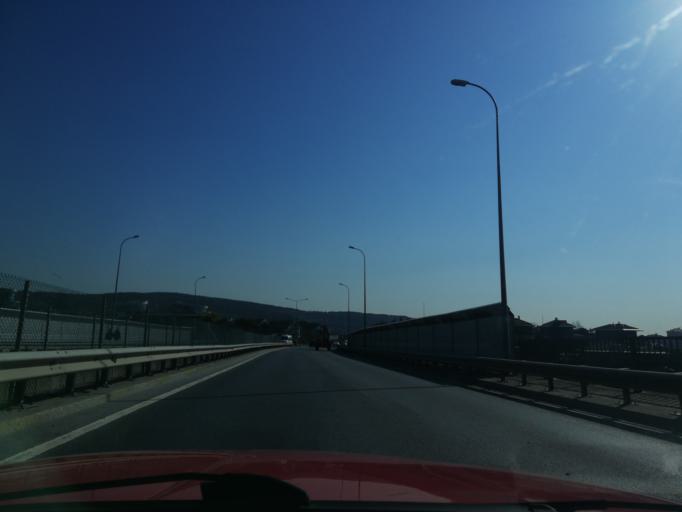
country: TR
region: Istanbul
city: Mahmut Sevket Pasa
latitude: 41.1141
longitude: 29.1188
